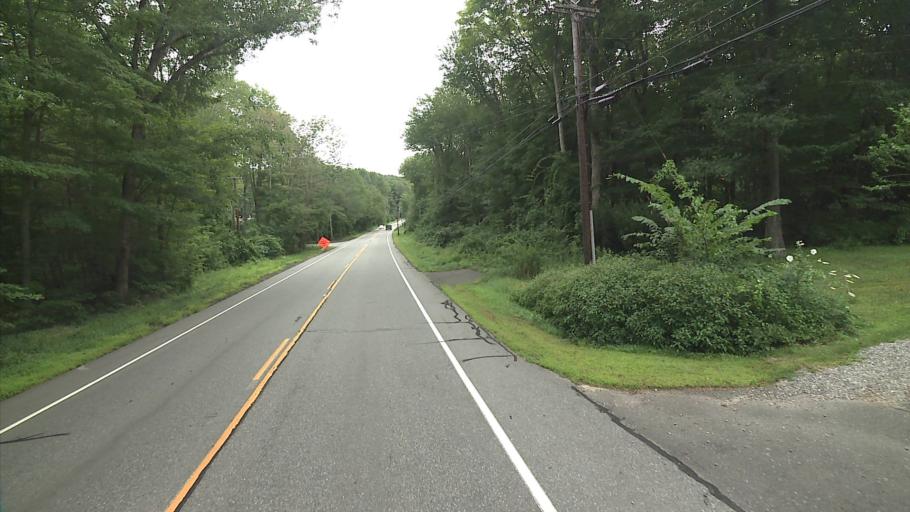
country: US
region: Connecticut
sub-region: Tolland County
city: Storrs
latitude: 41.8723
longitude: -72.2172
